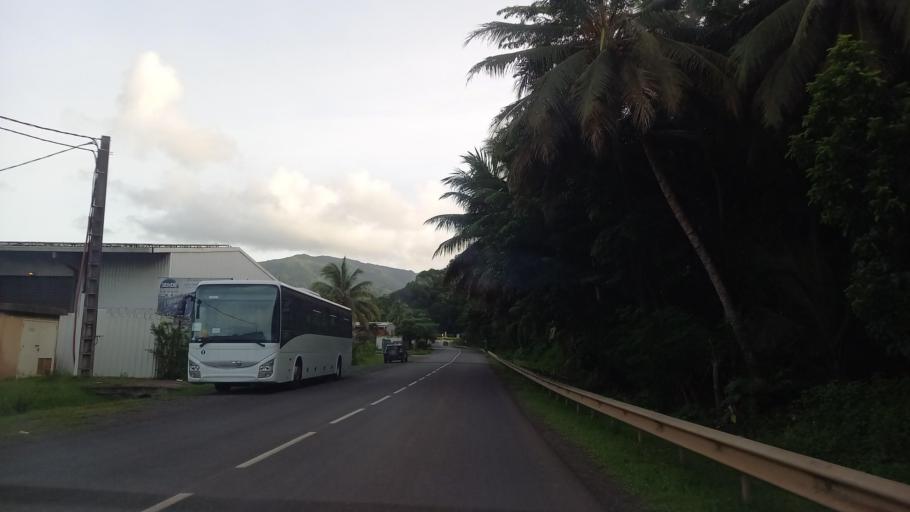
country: YT
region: Koungou
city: Koungou
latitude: -12.7266
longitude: 45.1696
